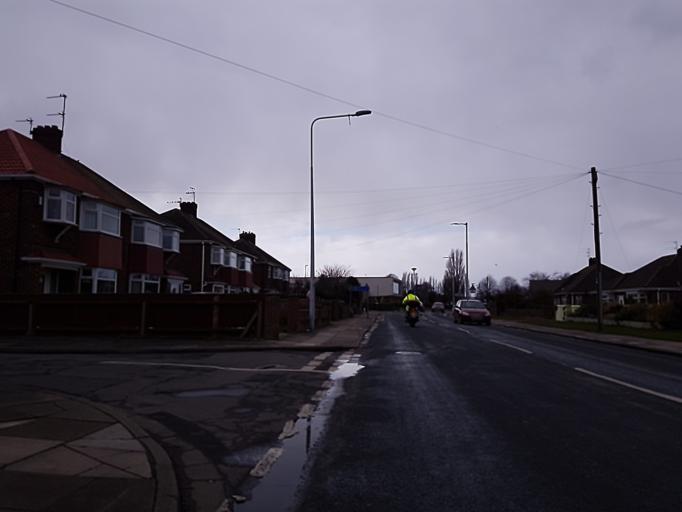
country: GB
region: England
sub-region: North East Lincolnshire
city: Grimbsy
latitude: 53.5561
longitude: -0.0970
